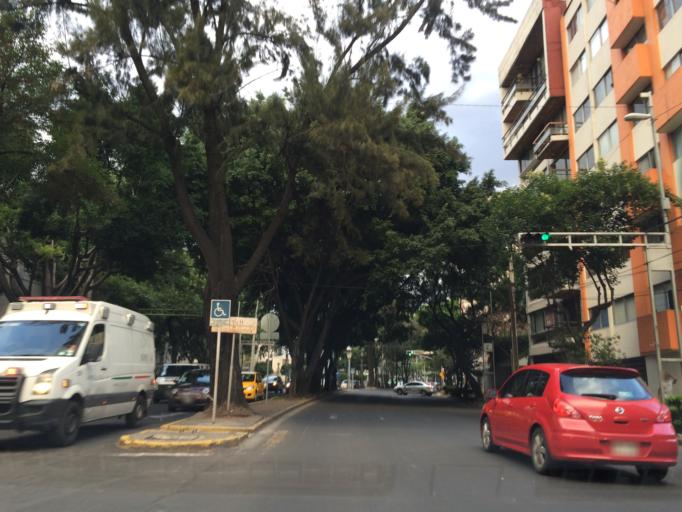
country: MX
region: Mexico City
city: Colonia del Valle
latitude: 19.3668
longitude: -99.1578
